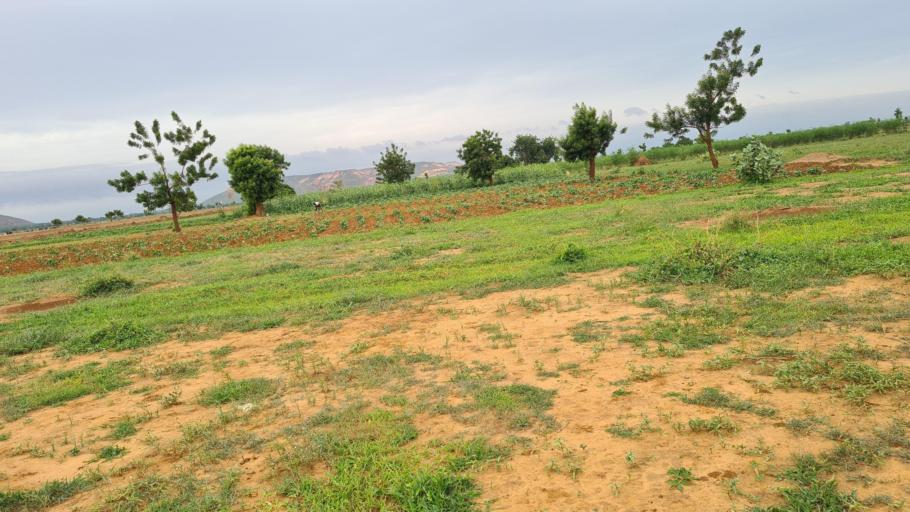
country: NE
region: Tahoua
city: Birni N Konni
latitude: 13.8396
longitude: 5.2700
